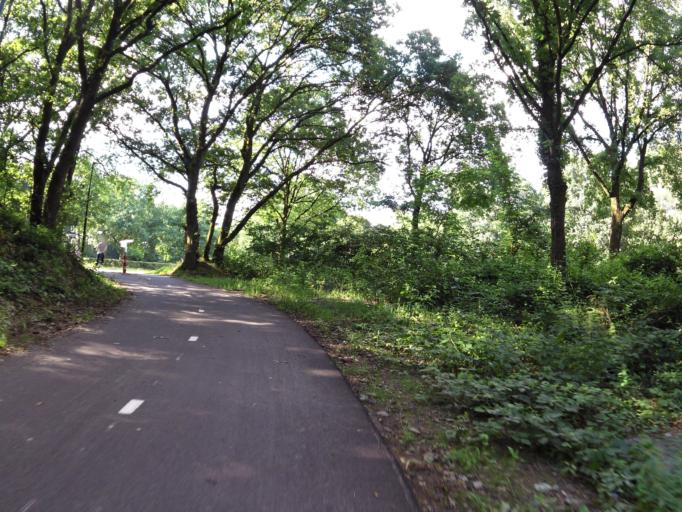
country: NL
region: North Brabant
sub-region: Gemeente Waalre
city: Waalre
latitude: 51.4009
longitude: 5.4616
